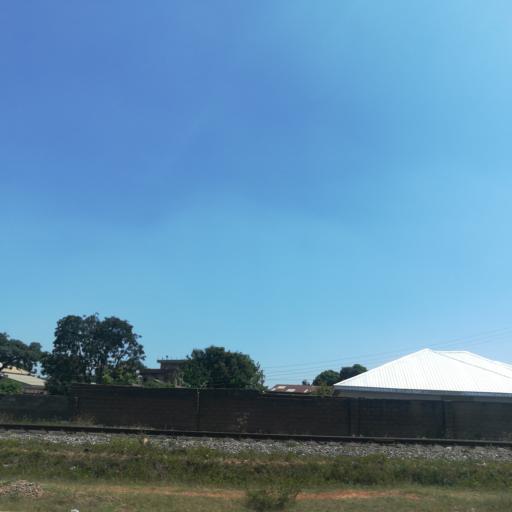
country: NG
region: Plateau
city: Bukuru
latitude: 9.8033
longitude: 8.8681
